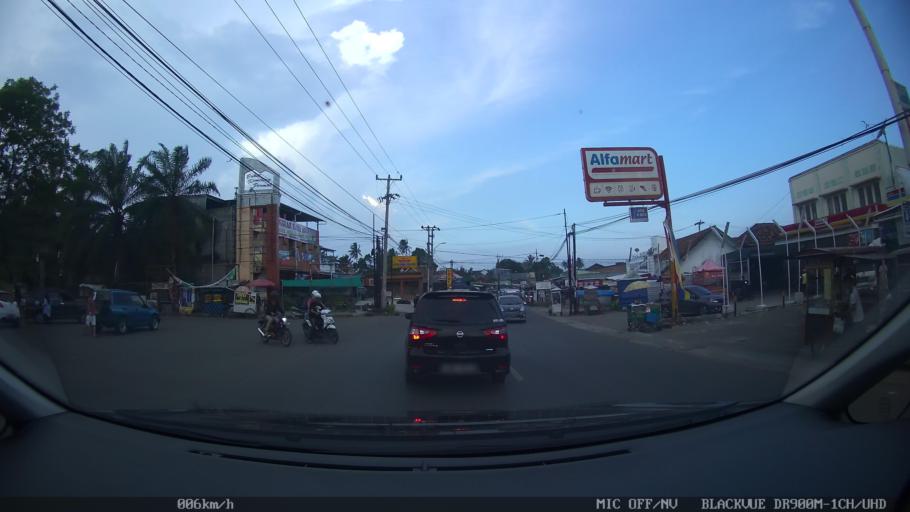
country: ID
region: Lampung
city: Kedaton
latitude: -5.3899
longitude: 105.2100
